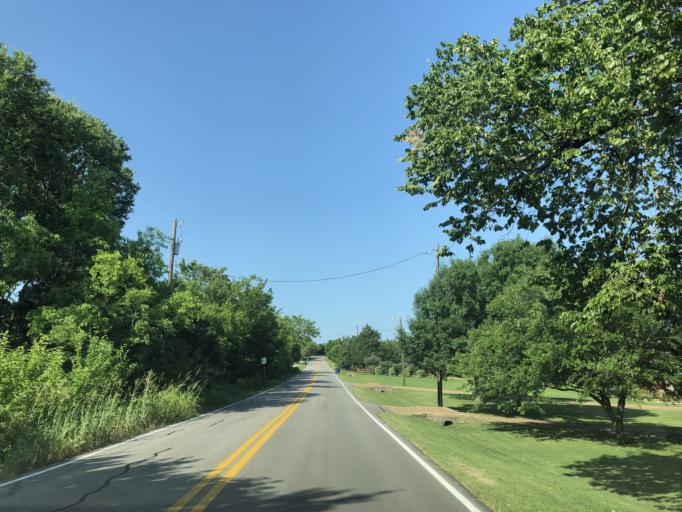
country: US
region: Texas
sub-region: Dallas County
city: Sunnyvale
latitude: 32.8273
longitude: -96.5828
